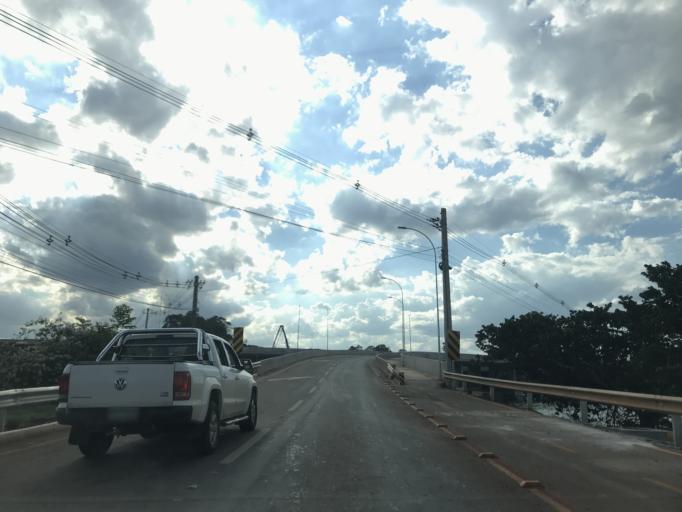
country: BR
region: Federal District
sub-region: Brasilia
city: Brasilia
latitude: -15.7311
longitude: -47.8926
